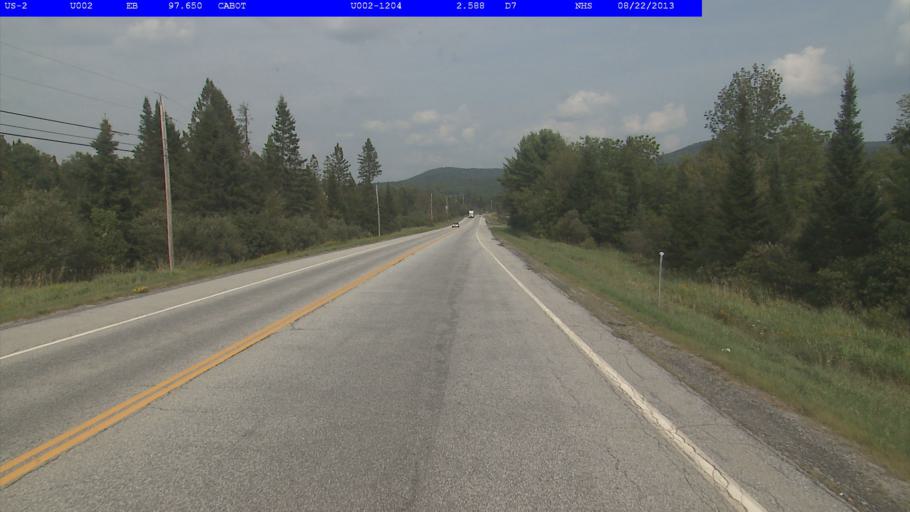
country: US
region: Vermont
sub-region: Caledonia County
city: Hardwick
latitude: 44.3692
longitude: -72.2756
